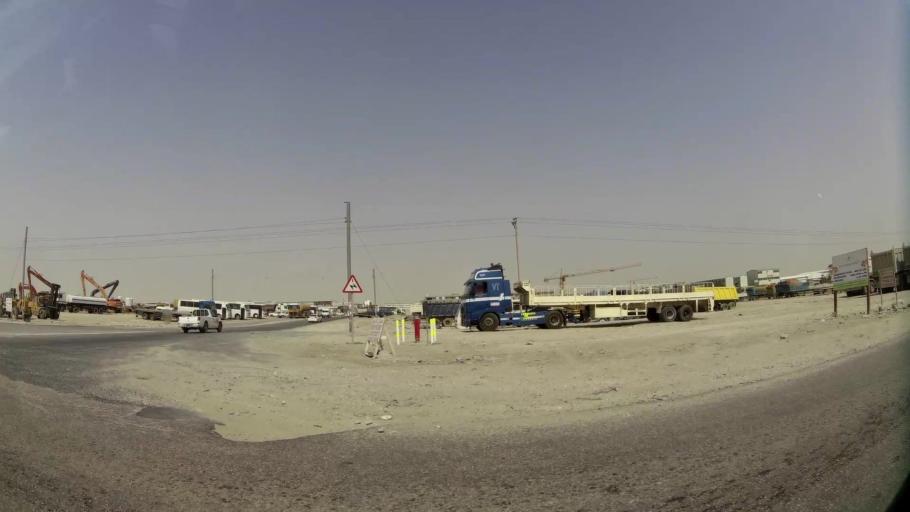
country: QA
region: Baladiyat ar Rayyan
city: Ar Rayyan
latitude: 25.2026
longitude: 51.3644
